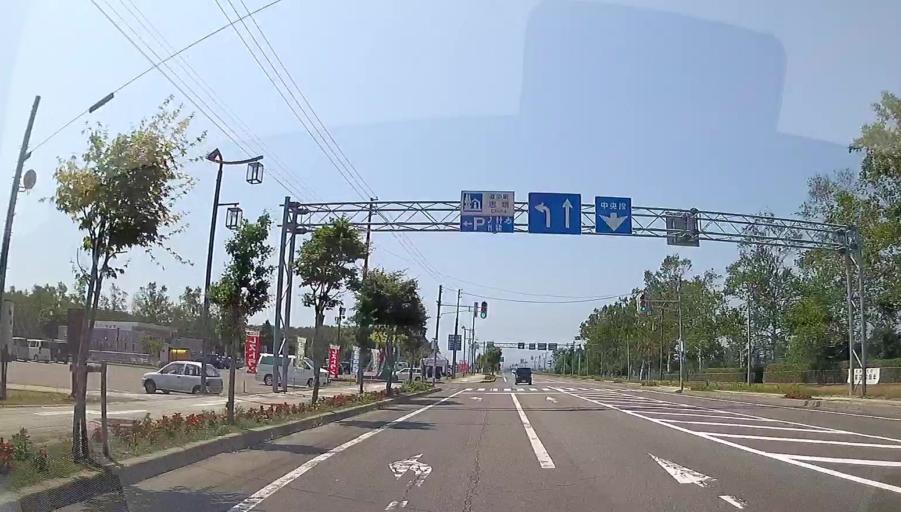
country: JP
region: Hokkaido
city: Obihiro
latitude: 42.5598
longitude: 143.2991
